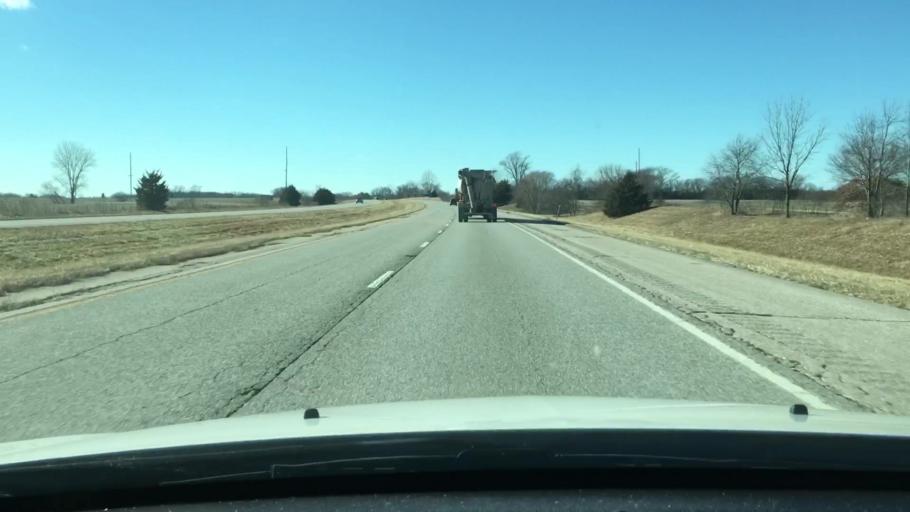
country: US
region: Illinois
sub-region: Pike County
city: Griggsville
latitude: 39.6784
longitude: -90.7198
